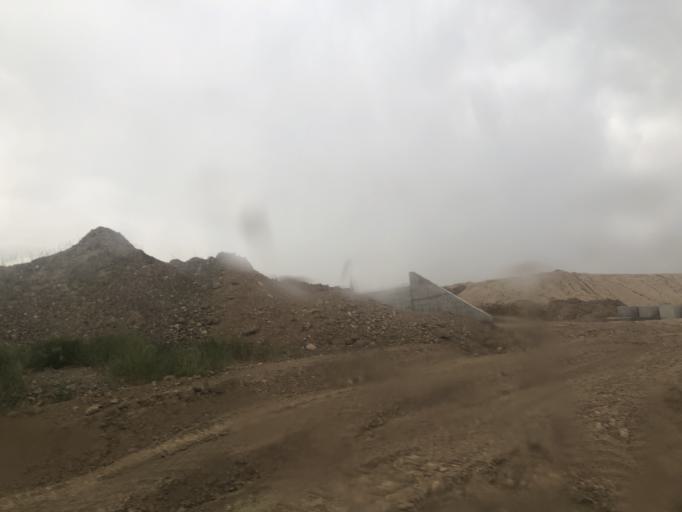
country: KG
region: Chuy
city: Bystrovka
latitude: 43.3264
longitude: 75.8489
